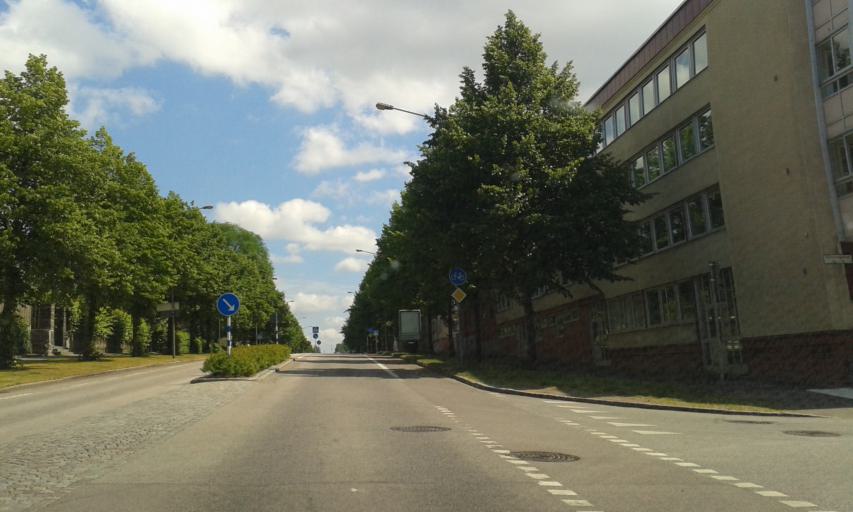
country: SE
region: Kronoberg
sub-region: Vaxjo Kommun
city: Vaexjoe
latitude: 56.8818
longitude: 14.8037
